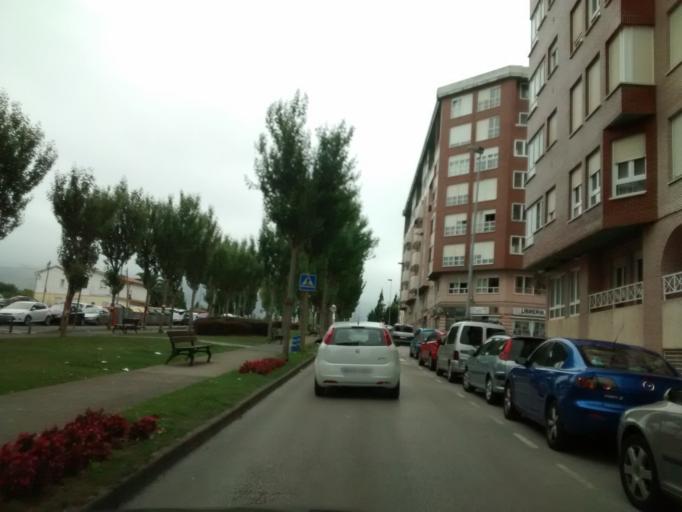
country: ES
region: Cantabria
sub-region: Provincia de Cantabria
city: Torrelavega
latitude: 43.3394
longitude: -4.0496
